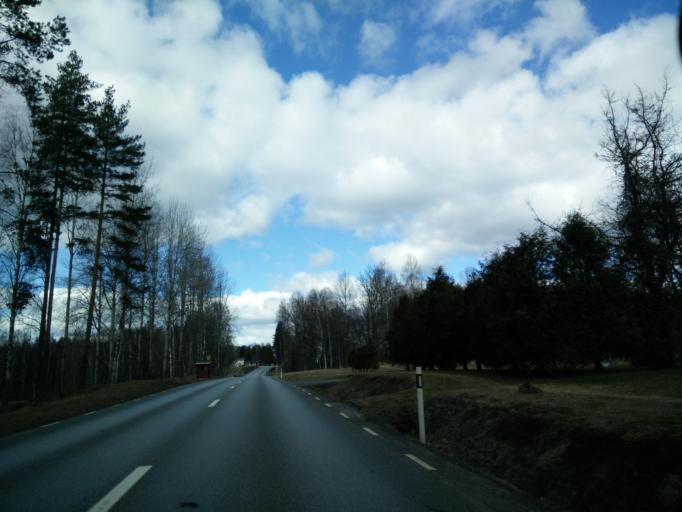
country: SE
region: Vaermland
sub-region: Munkfors Kommun
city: Munkfors
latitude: 59.8951
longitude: 13.5606
